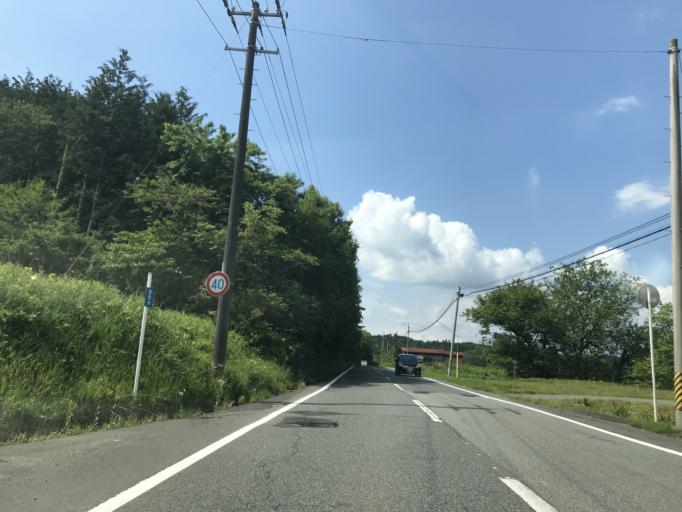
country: JP
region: Miyagi
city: Furukawa
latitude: 38.7274
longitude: 140.9529
